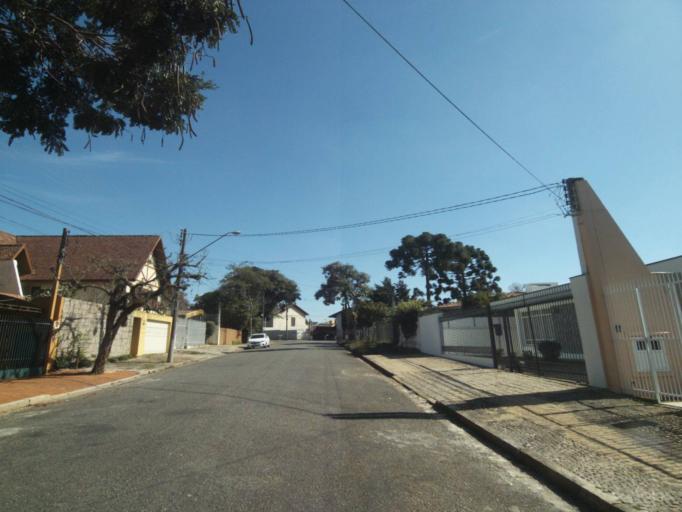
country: BR
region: Parana
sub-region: Curitiba
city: Curitiba
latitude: -25.4181
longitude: -49.2341
